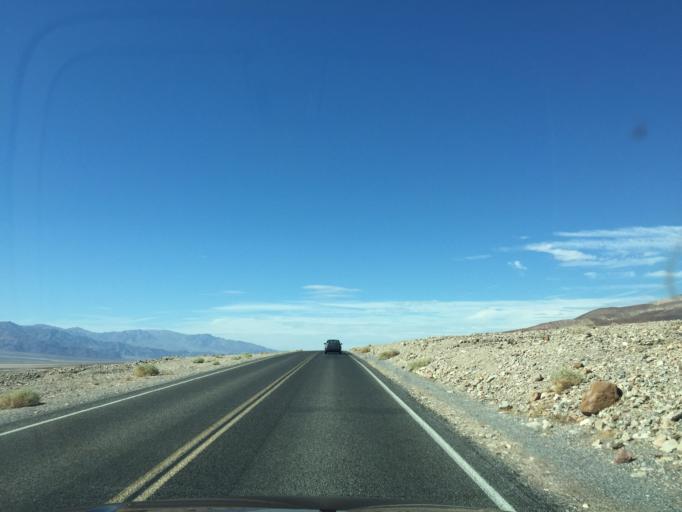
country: US
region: Nevada
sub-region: Nye County
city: Beatty
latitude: 36.2572
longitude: -116.7769
